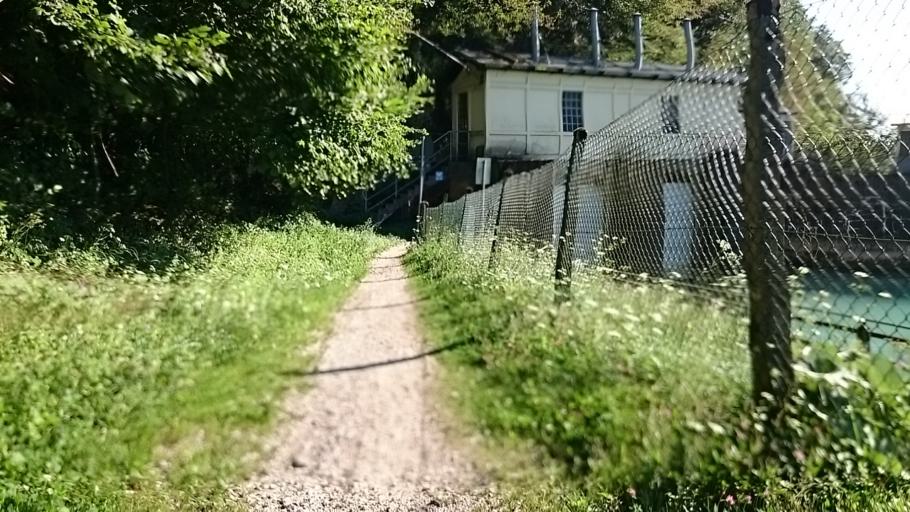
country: IT
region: Veneto
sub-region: Provincia di Belluno
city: Soverzene
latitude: 46.1987
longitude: 12.3018
